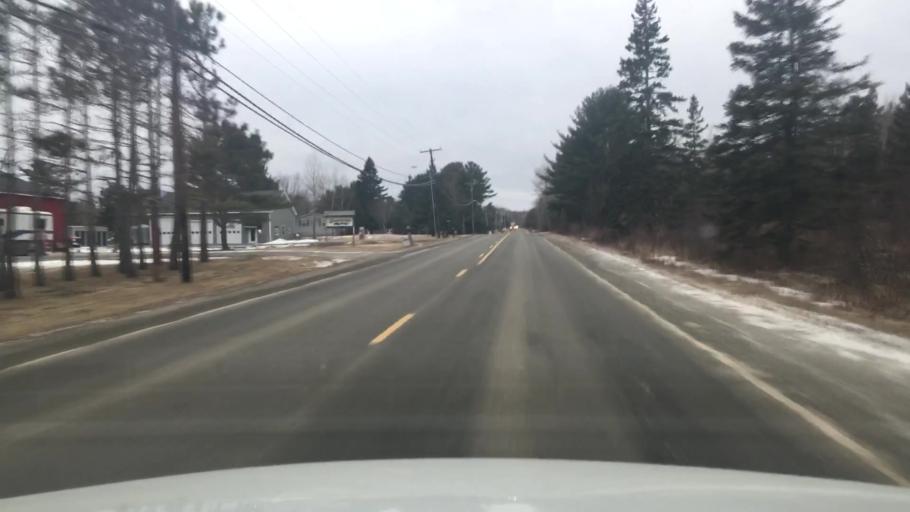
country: US
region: Maine
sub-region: Hancock County
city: Trenton
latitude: 44.5005
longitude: -68.3509
